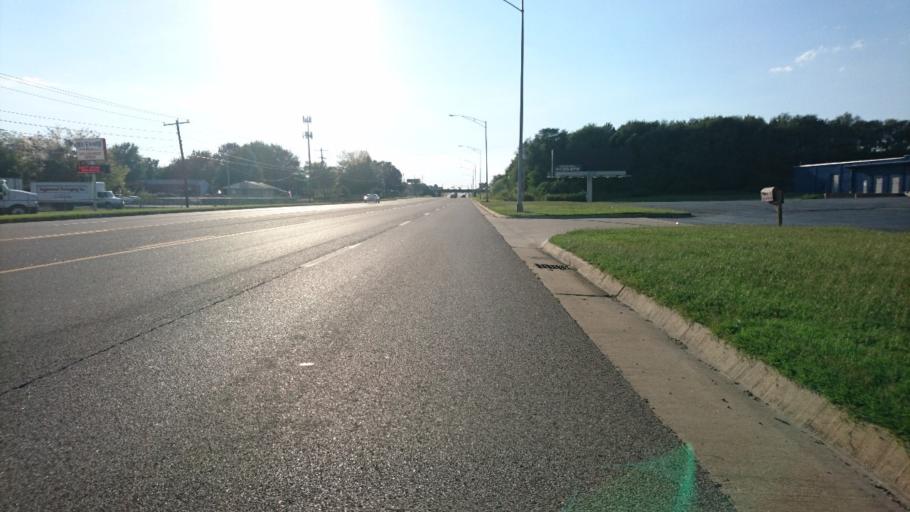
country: US
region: Missouri
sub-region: Greene County
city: Springfield
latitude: 37.2125
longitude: -93.3739
